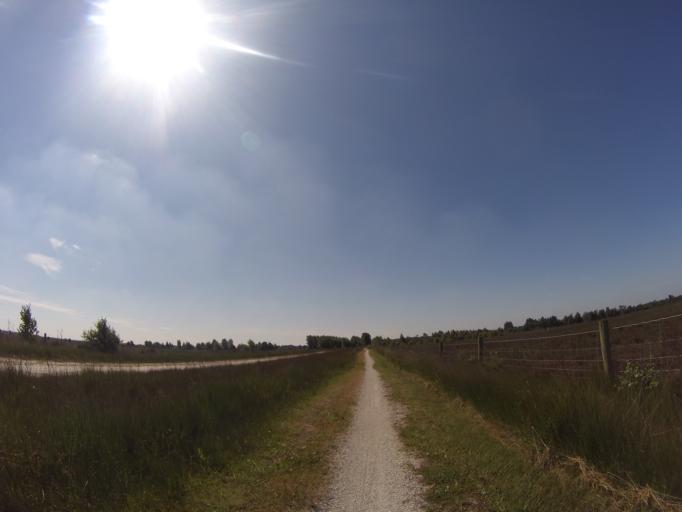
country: DE
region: Lower Saxony
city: Twist
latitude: 52.6801
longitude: 7.0231
